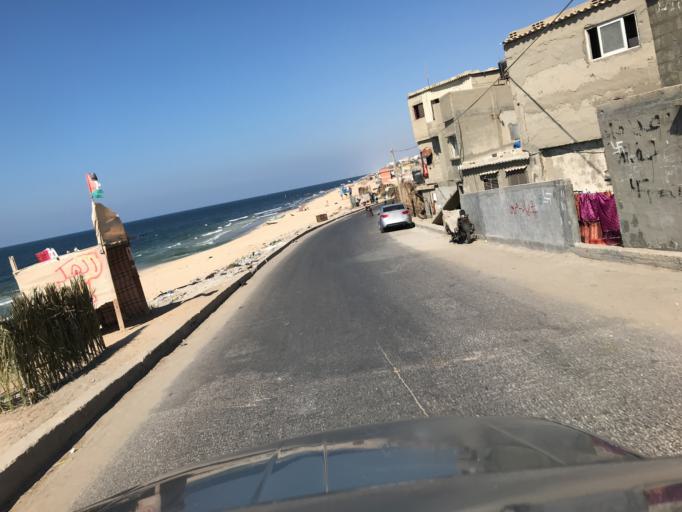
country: PS
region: Gaza Strip
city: Dayr al Balah
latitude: 31.4278
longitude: 34.3408
